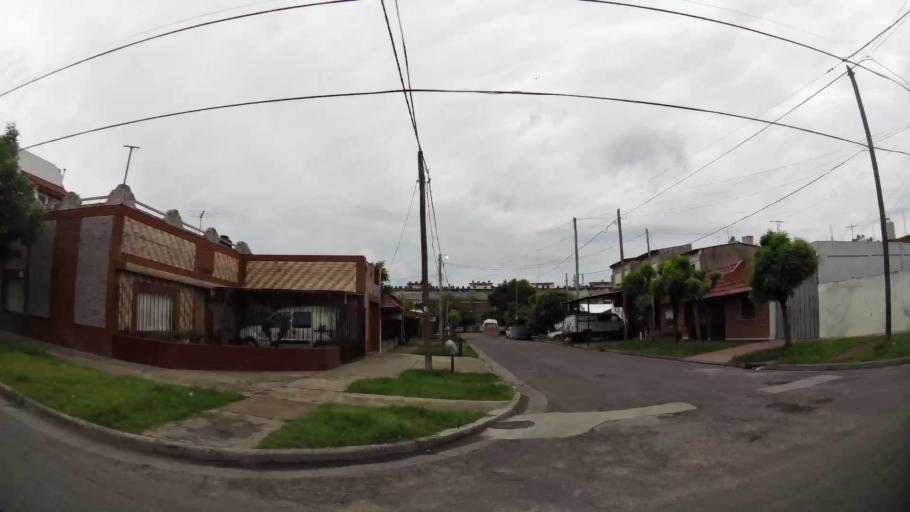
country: AR
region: Buenos Aires
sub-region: Partido de Lanus
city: Lanus
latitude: -34.7370
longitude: -58.3597
